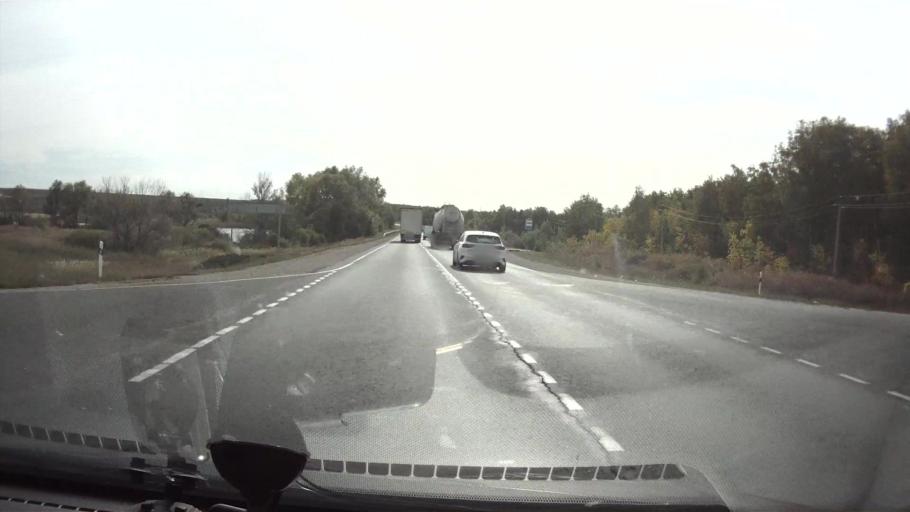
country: RU
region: Saratov
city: Alekseyevka
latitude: 52.2495
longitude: 47.9113
